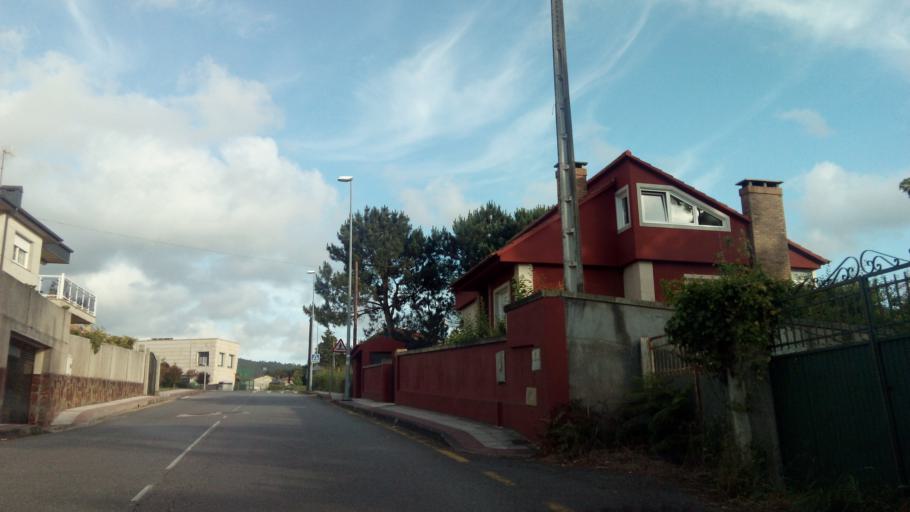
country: ES
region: Galicia
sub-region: Provincia de Pontevedra
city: Nigran
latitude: 42.1107
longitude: -8.8163
